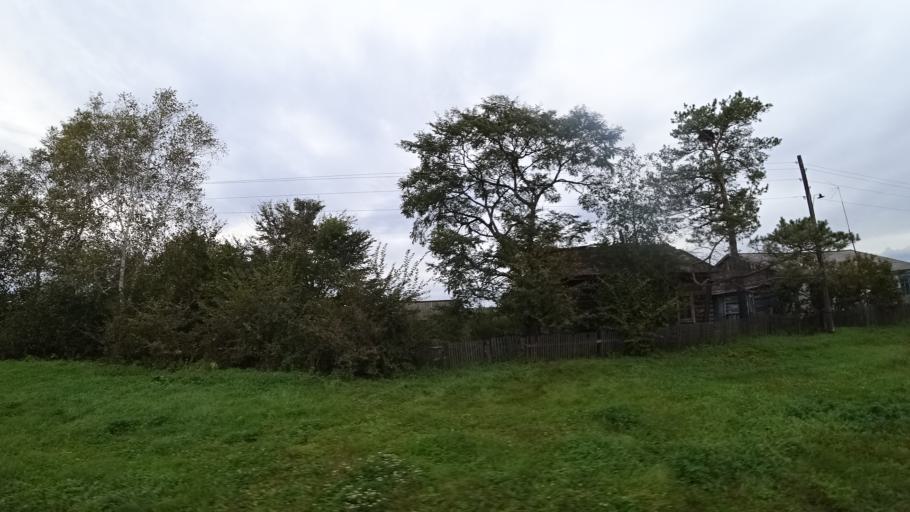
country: RU
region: Amur
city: Arkhara
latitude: 49.4334
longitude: 130.2624
